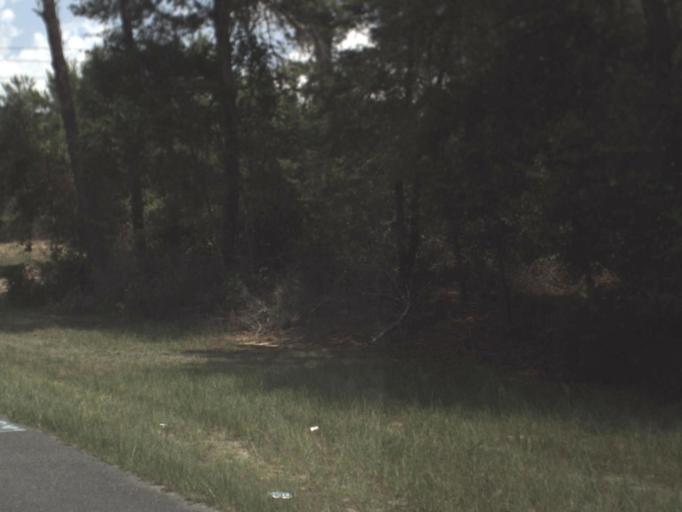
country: US
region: Florida
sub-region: Putnam County
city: Crescent City
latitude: 29.3697
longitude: -81.7357
